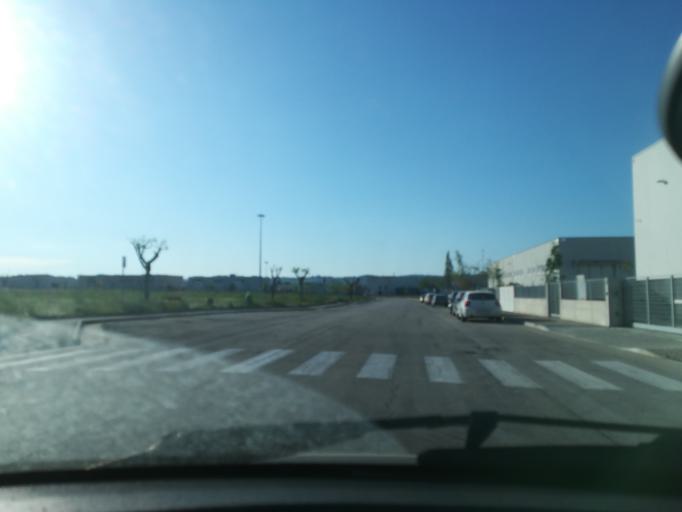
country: IT
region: The Marches
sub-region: Provincia di Macerata
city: Zona Industriale
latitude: 43.2600
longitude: 13.4863
